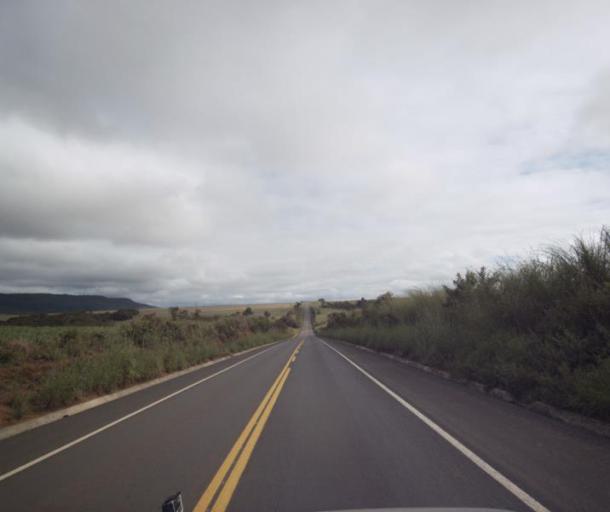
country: BR
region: Goias
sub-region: Padre Bernardo
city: Padre Bernardo
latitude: -15.3982
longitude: -48.6340
